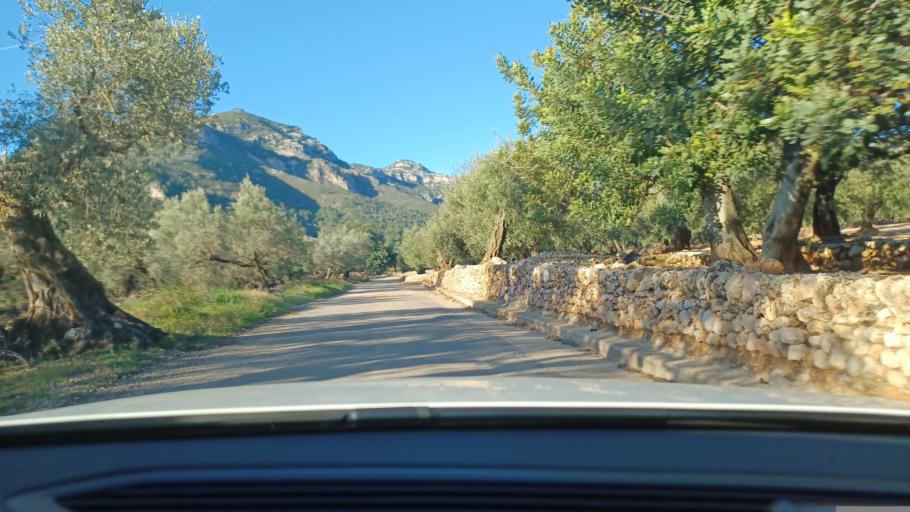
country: ES
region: Catalonia
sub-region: Provincia de Tarragona
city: Mas de Barberans
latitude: 40.7172
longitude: 0.3562
